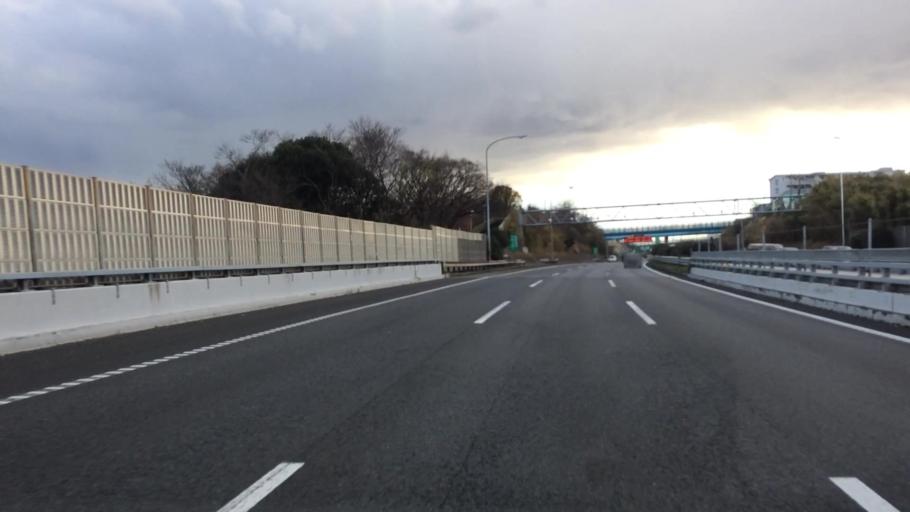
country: JP
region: Kanagawa
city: Yokohama
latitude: 35.4927
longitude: 139.5924
